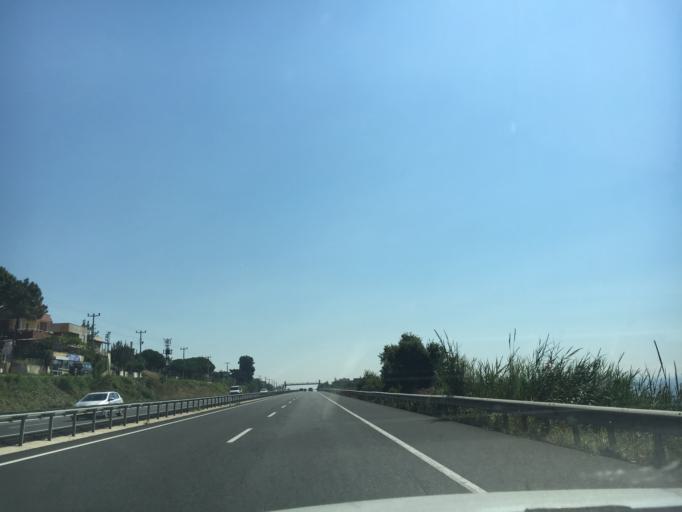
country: TR
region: Tekirdag
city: Marmara Ereglisi
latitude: 40.9696
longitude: 27.9050
